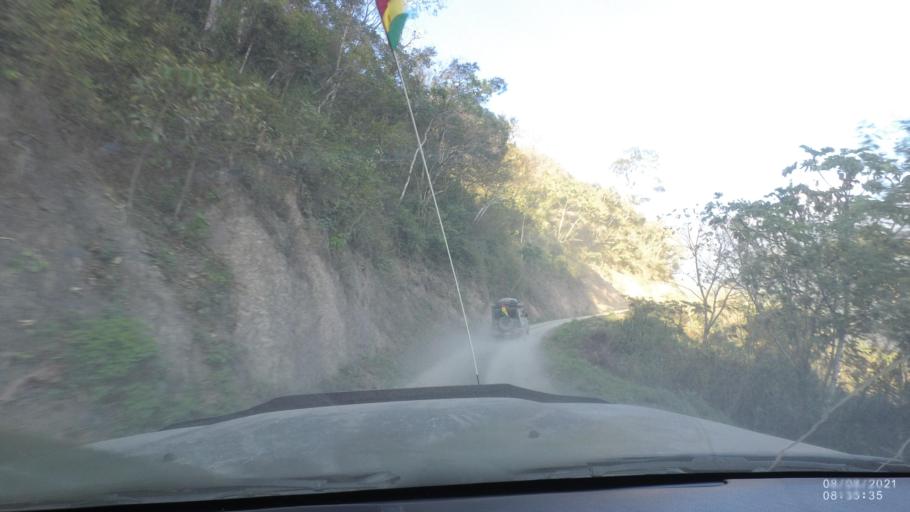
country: BO
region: La Paz
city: Quime
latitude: -16.5165
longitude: -66.7669
